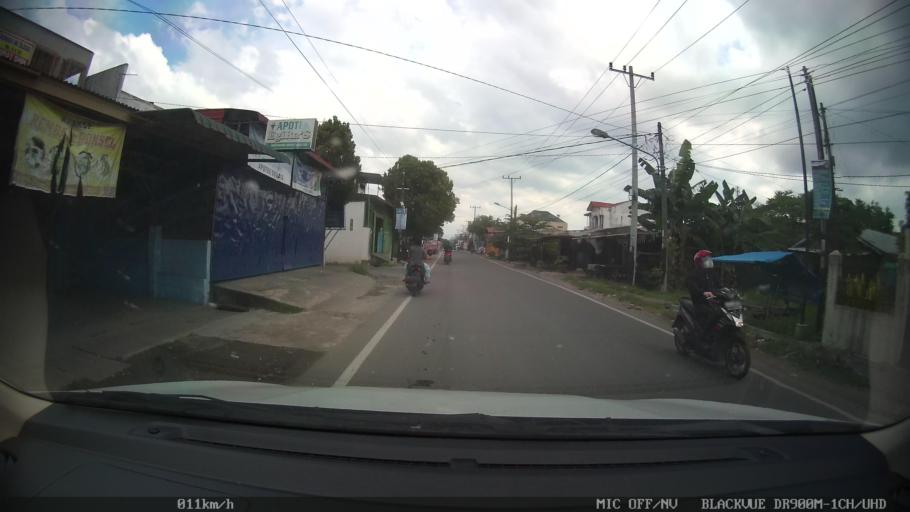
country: ID
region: North Sumatra
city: Sunggal
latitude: 3.6184
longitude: 98.6243
